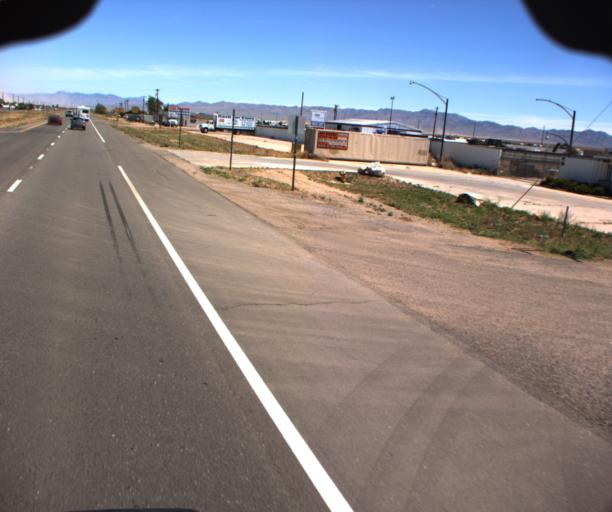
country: US
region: Arizona
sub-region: Mohave County
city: New Kingman-Butler
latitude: 35.2346
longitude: -113.9937
